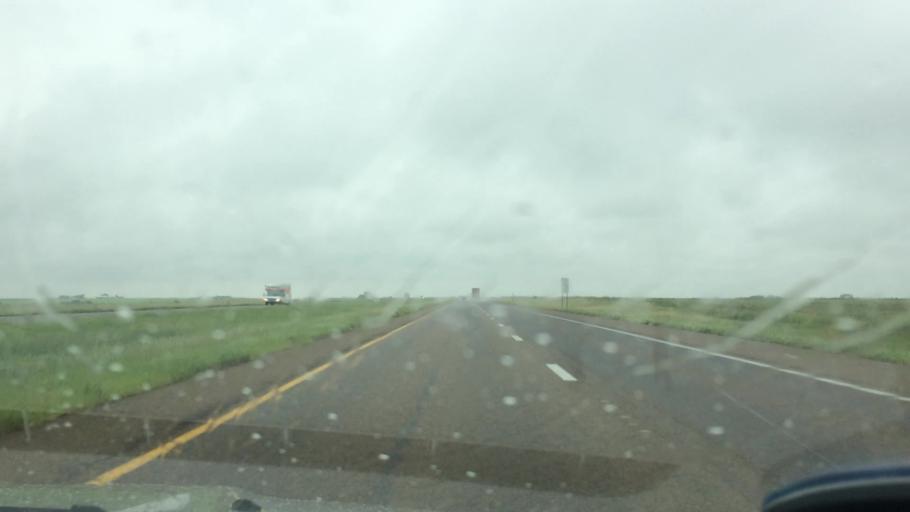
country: US
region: Kansas
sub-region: Ellis County
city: Victoria
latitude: 38.8638
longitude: -99.0305
